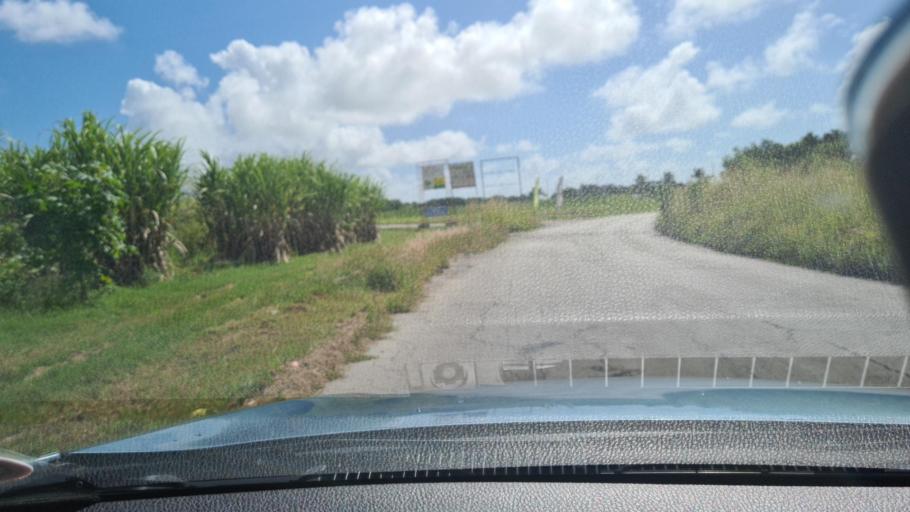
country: BB
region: Christ Church
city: Oistins
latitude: 13.0846
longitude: -59.5363
